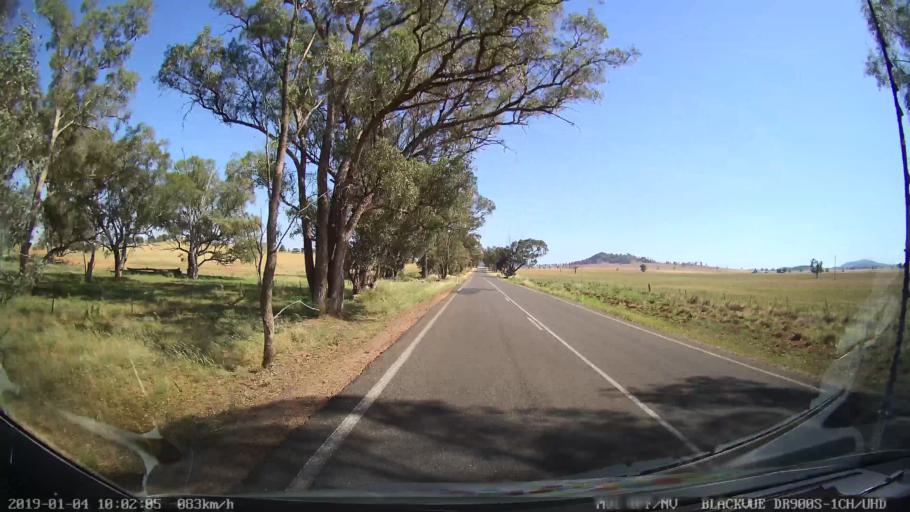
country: AU
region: New South Wales
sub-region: Cabonne
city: Canowindra
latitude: -33.4807
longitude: 148.3661
